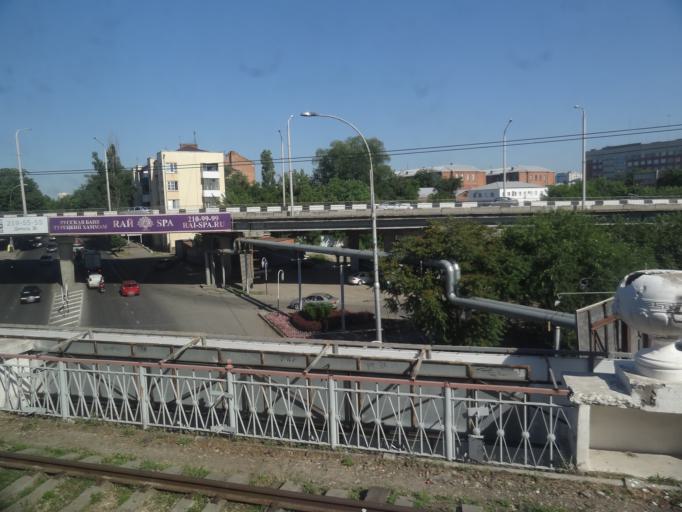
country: RU
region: Krasnodarskiy
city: Krasnodar
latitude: 45.0133
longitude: 38.9766
